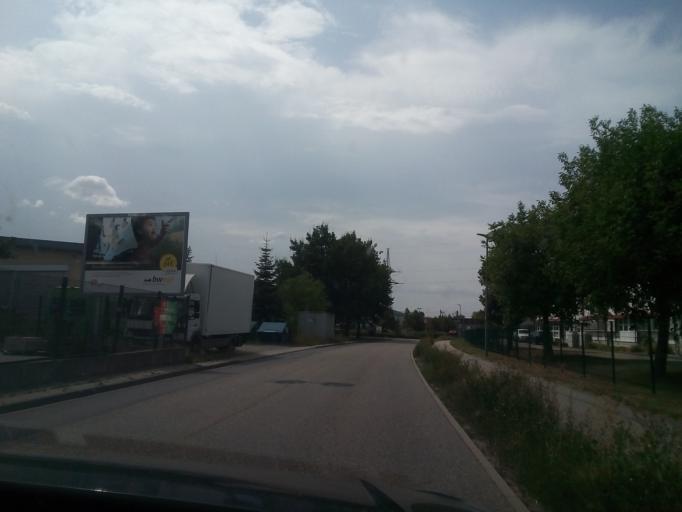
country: DE
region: Baden-Wuerttemberg
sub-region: Karlsruhe Region
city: Kuppenheim
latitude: 48.8127
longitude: 8.2128
